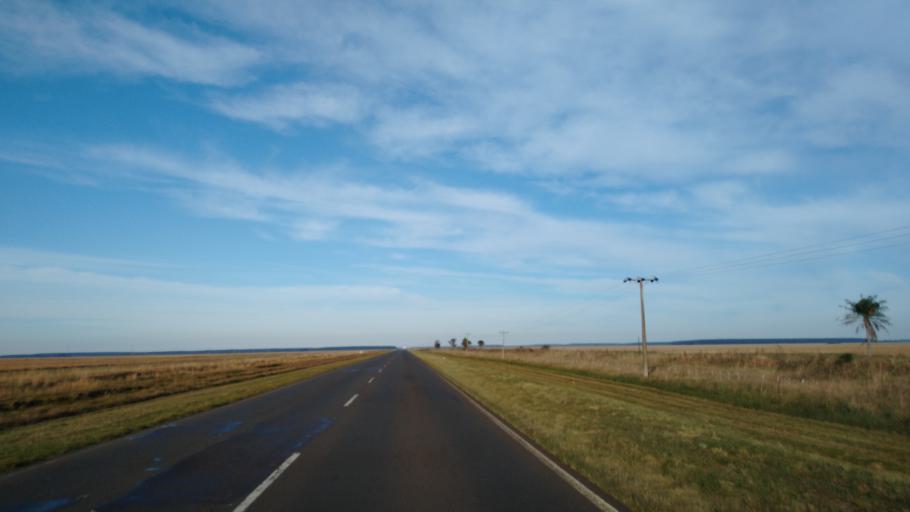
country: AR
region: Corrientes
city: La Cruz
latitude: -29.2672
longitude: -56.7525
